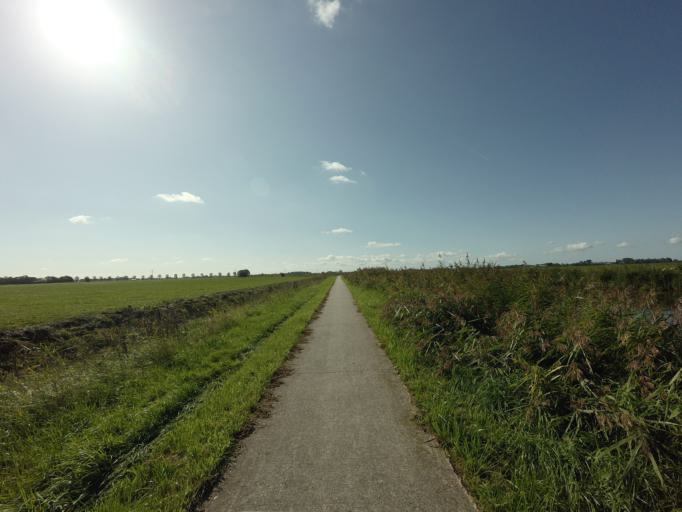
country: NL
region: Friesland
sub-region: Gemeente Boarnsterhim
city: Reduzum
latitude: 53.1261
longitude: 5.7552
